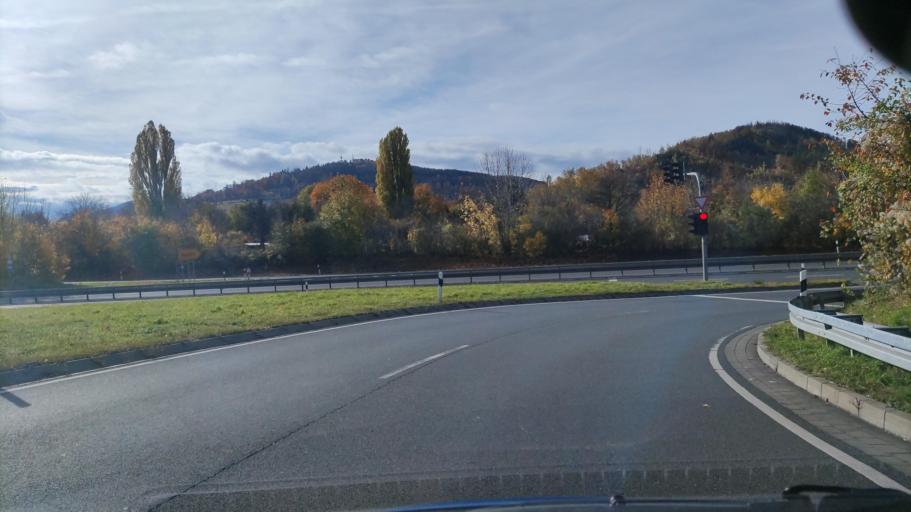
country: DE
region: Lower Saxony
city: Goslar
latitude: 51.9211
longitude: 10.4133
